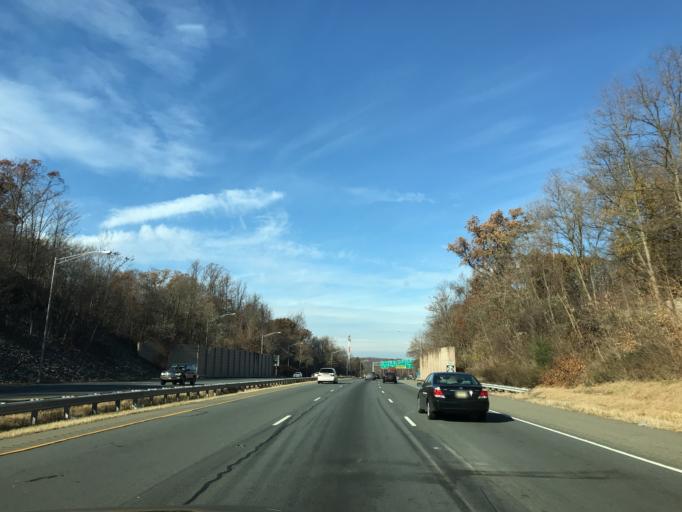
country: US
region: New Jersey
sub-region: Morris County
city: Morristown
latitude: 40.8008
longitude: -74.4418
